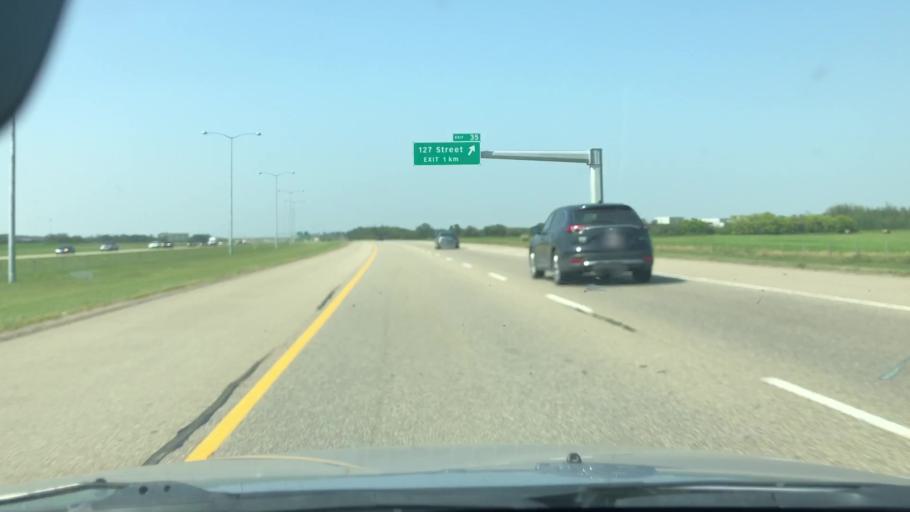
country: CA
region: Alberta
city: Edmonton
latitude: 53.6455
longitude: -113.5236
